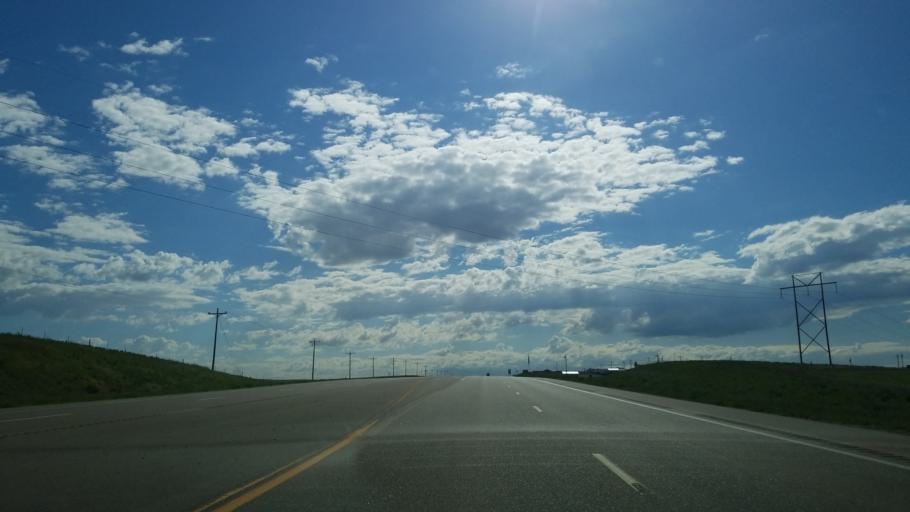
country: US
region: North Dakota
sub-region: McKenzie County
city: Watford City
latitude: 47.8049
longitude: -103.6094
